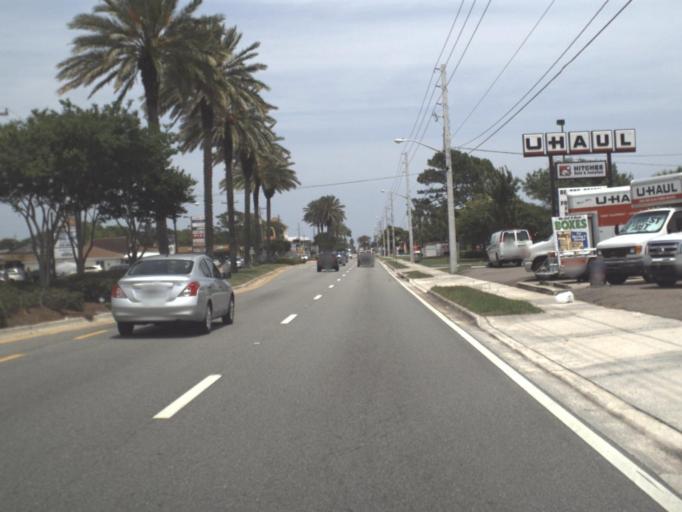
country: US
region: Florida
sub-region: Duval County
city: Atlantic Beach
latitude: 30.3245
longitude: -81.4039
